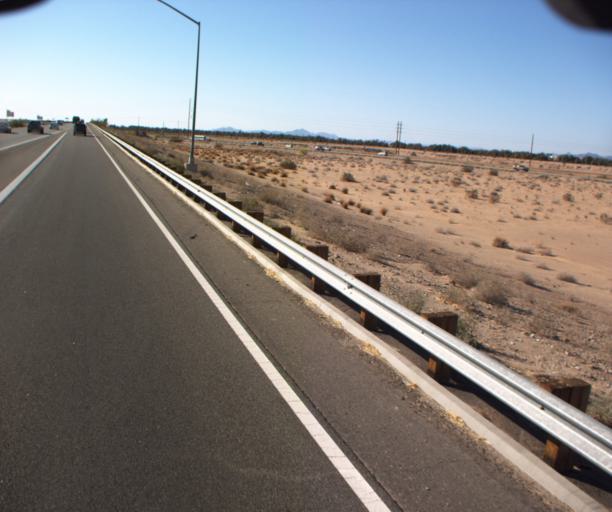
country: US
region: Arizona
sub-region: Yuma County
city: Fortuna Foothills
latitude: 32.6727
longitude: -114.4872
